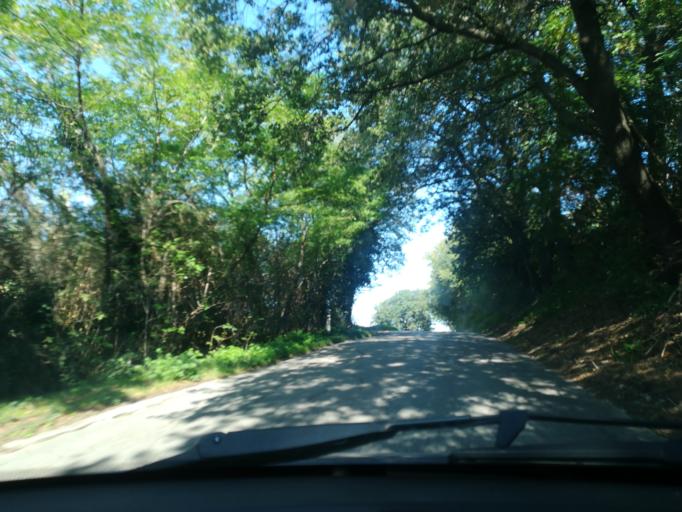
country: IT
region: The Marches
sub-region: Provincia di Macerata
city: Sforzacosta
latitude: 43.2665
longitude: 13.4525
